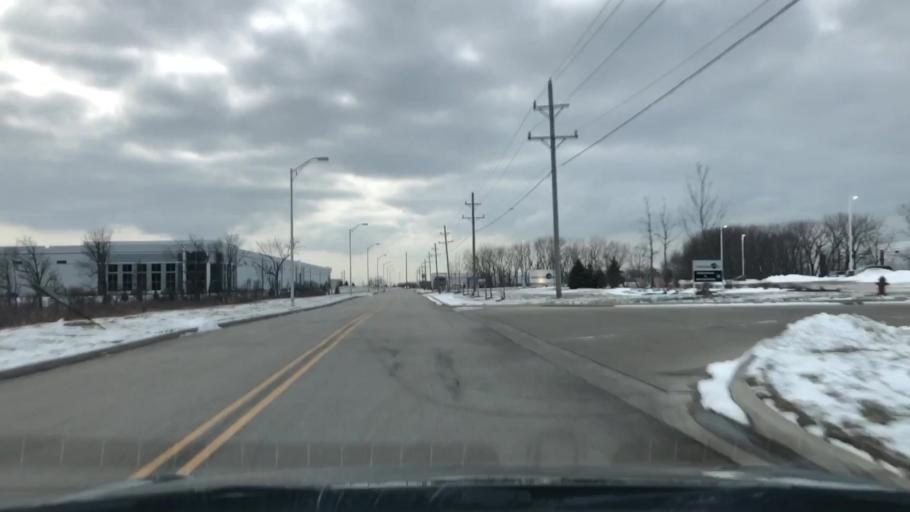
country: US
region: Illinois
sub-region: Cook County
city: Lemont
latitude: 41.6203
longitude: -88.0010
